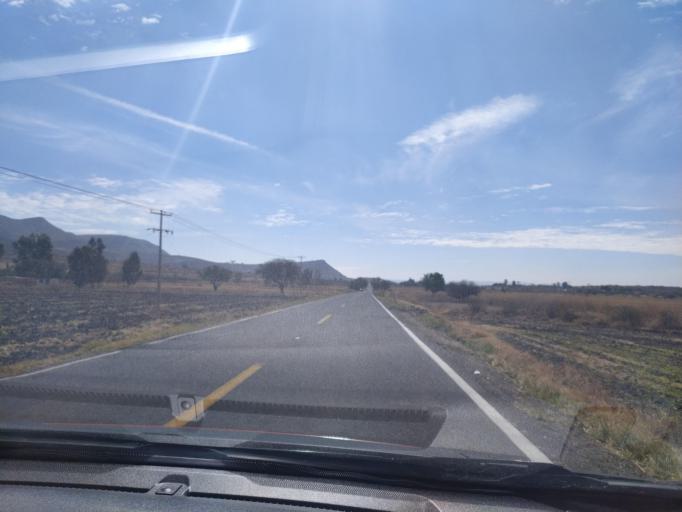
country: MX
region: Guanajuato
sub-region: San Francisco del Rincon
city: San Ignacio de Hidalgo
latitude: 20.8338
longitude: -101.8452
